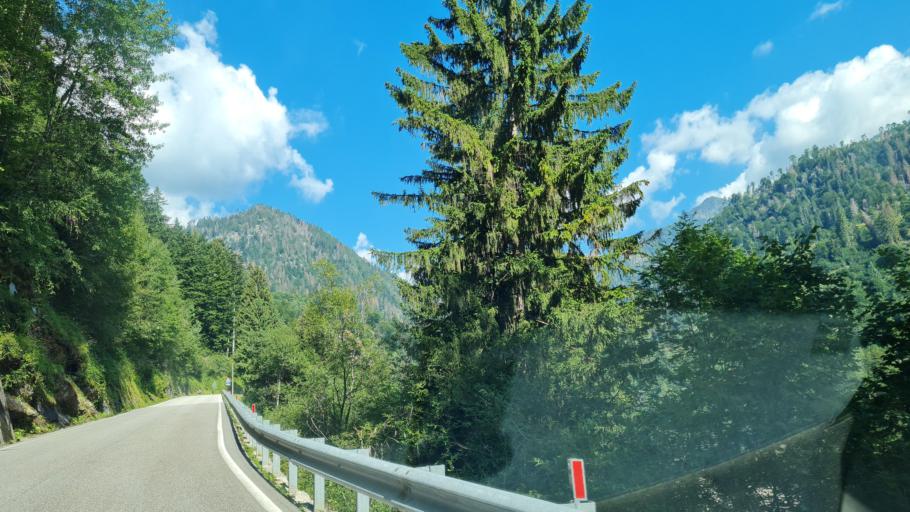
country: IT
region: Trentino-Alto Adige
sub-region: Provincia di Trento
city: Carzano
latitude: 46.1185
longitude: 11.4866
